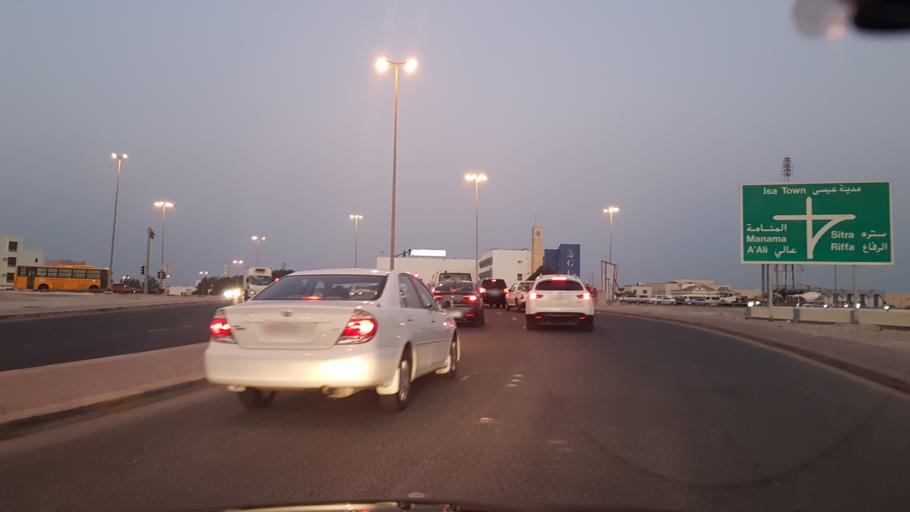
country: BH
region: Northern
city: Ar Rifa'
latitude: 26.1507
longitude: 50.5730
